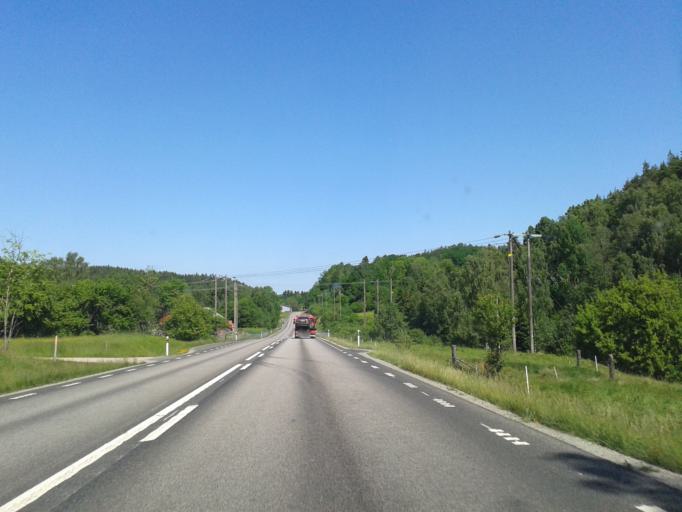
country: SE
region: Vaestra Goetaland
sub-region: Orust
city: Henan
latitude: 58.2174
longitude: 11.6901
